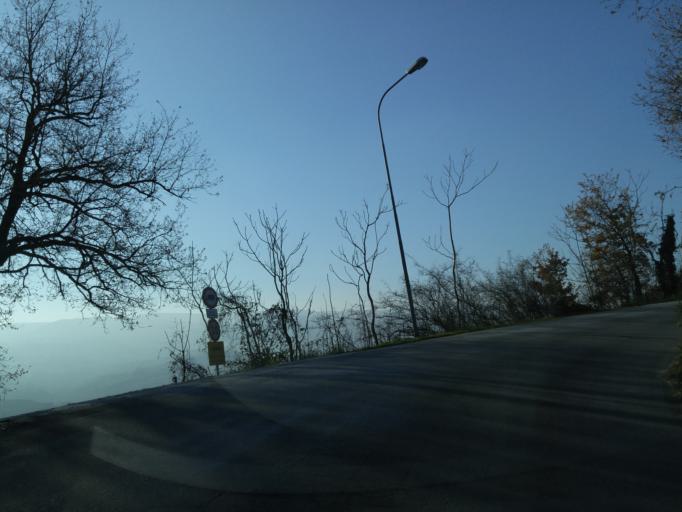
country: IT
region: The Marches
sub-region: Provincia di Pesaro e Urbino
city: Montefelcino
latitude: 43.7325
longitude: 12.8357
